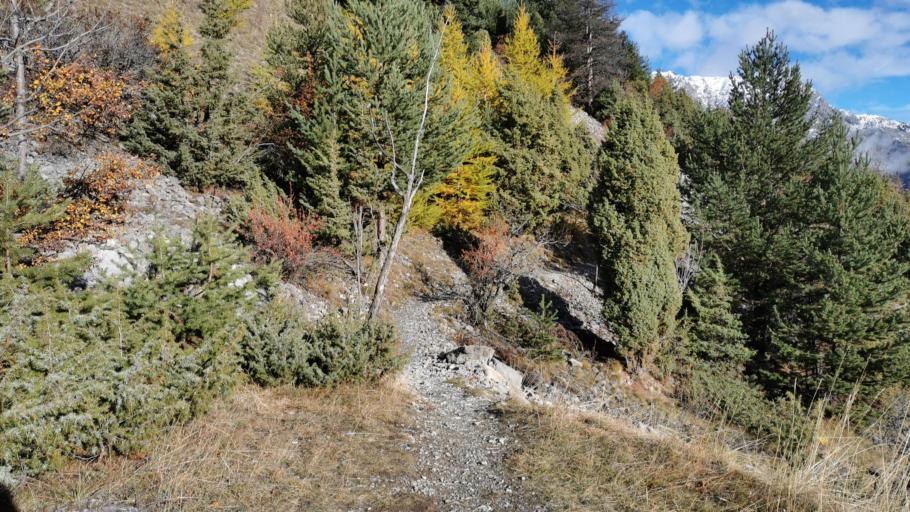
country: IT
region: Piedmont
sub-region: Provincia di Torino
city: Bardonecchia
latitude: 45.0238
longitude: 6.6197
